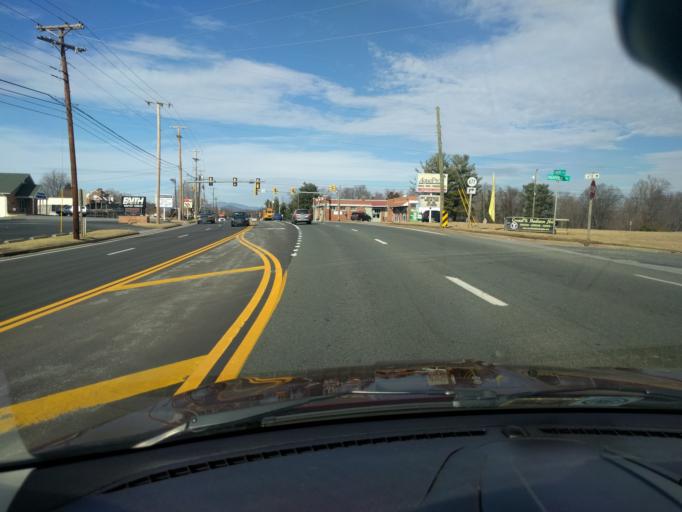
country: US
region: Virginia
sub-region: Amherst County
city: Madison Heights
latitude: 37.4772
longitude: -79.1181
